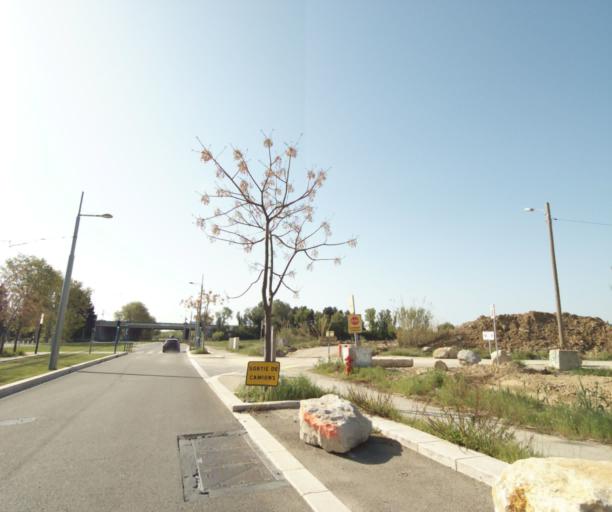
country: FR
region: Languedoc-Roussillon
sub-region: Departement de l'Herault
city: Lattes
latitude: 43.5956
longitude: 3.9049
